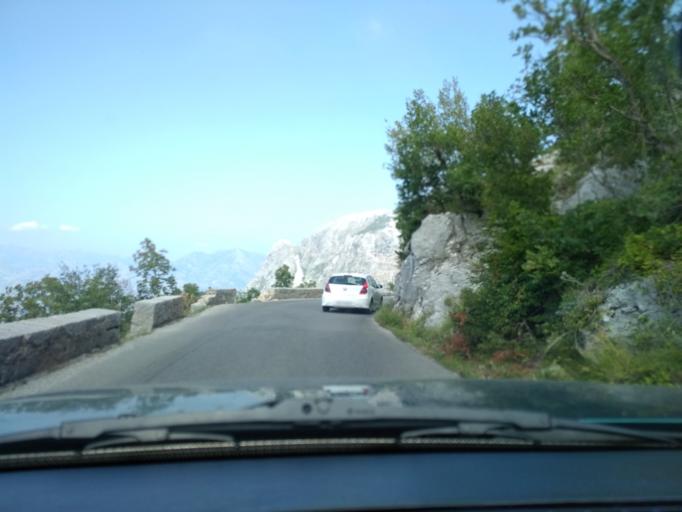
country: ME
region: Kotor
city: Kotor
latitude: 42.4148
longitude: 18.7918
